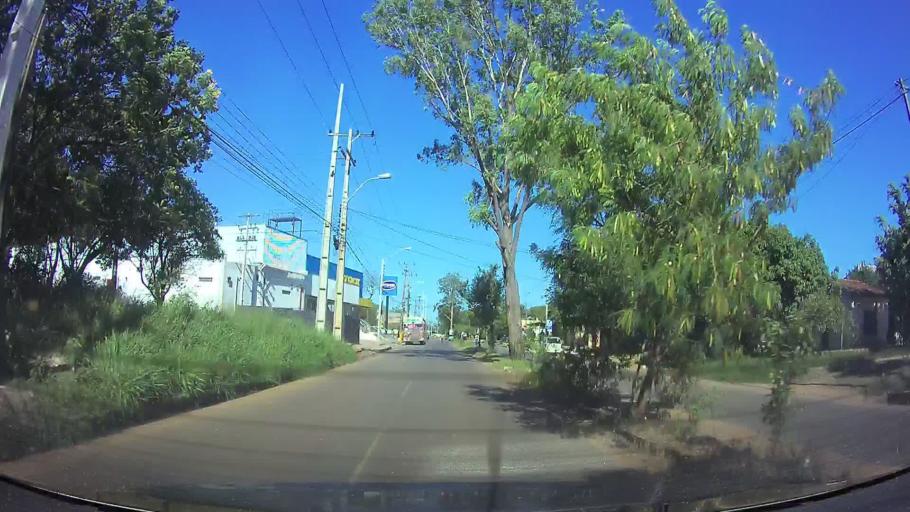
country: PY
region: Central
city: Fernando de la Mora
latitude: -25.2966
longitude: -57.5238
